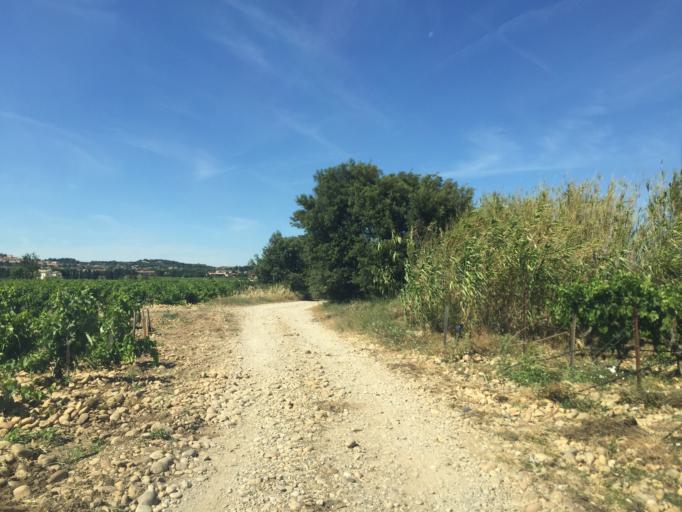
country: FR
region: Provence-Alpes-Cote d'Azur
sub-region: Departement du Vaucluse
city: Chateauneuf-du-Pape
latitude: 44.0387
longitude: 4.8351
